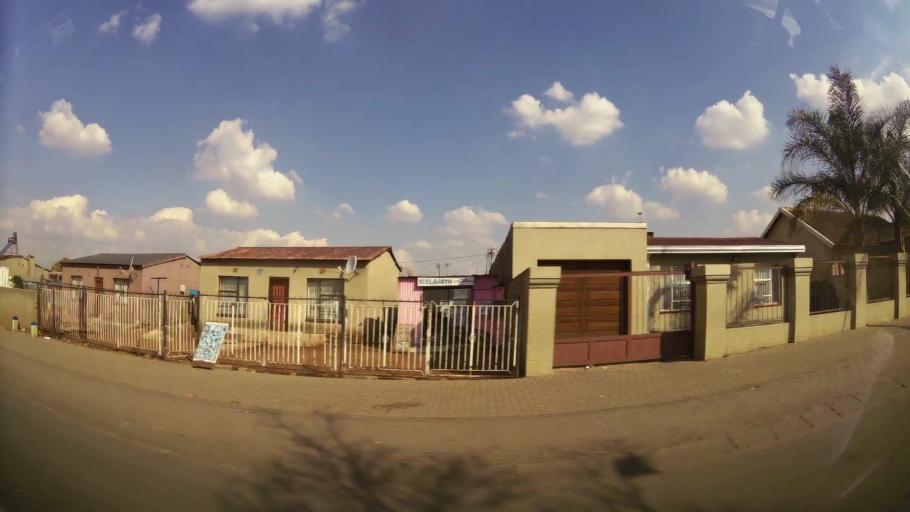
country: ZA
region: Gauteng
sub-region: Ekurhuleni Metropolitan Municipality
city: Germiston
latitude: -26.3276
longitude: 28.1494
